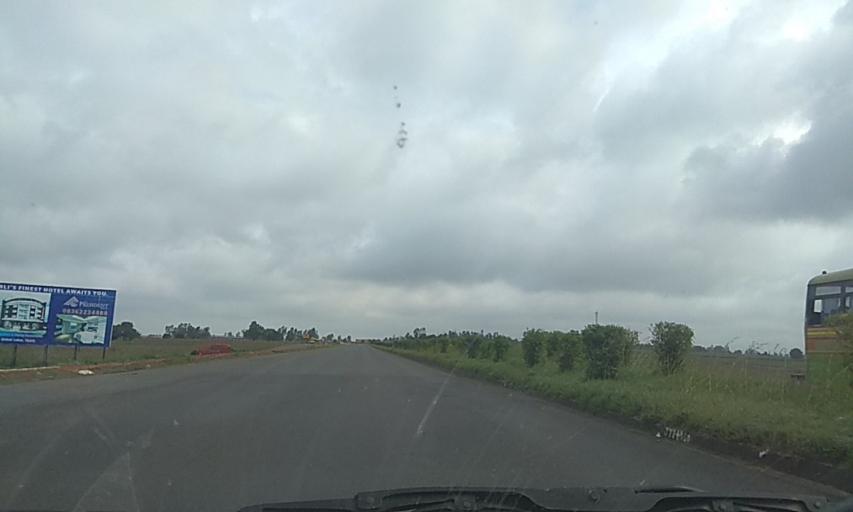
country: IN
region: Karnataka
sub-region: Haveri
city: Shiggaon
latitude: 15.0937
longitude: 75.1521
